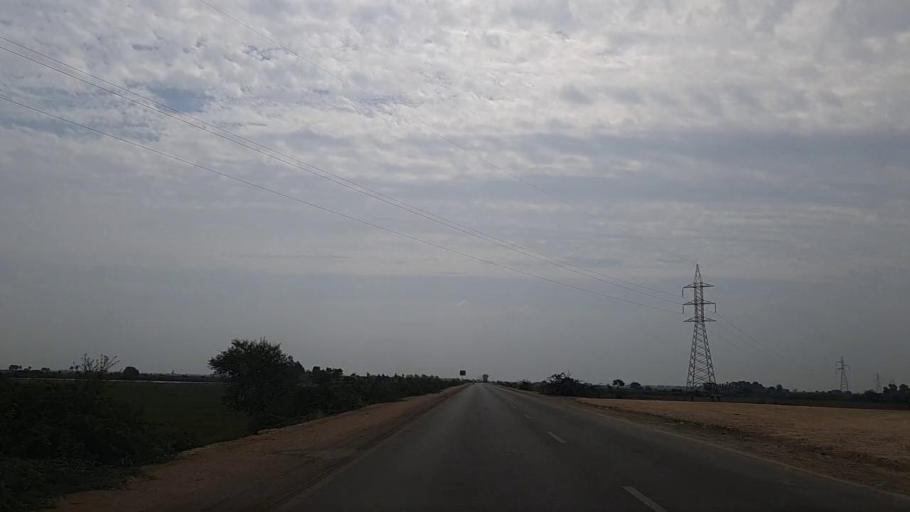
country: PK
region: Sindh
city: Daro Mehar
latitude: 24.6126
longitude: 68.0902
